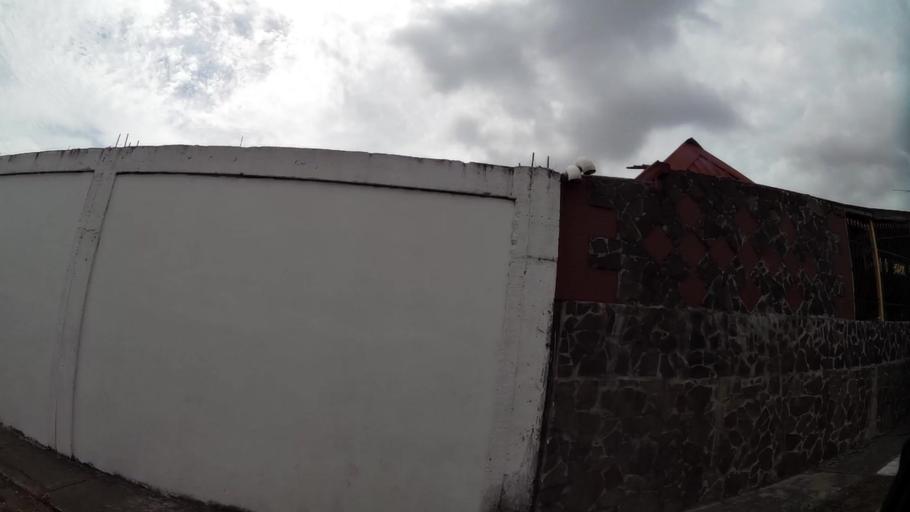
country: PA
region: Panama
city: San Miguelito
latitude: 9.0527
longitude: -79.4200
